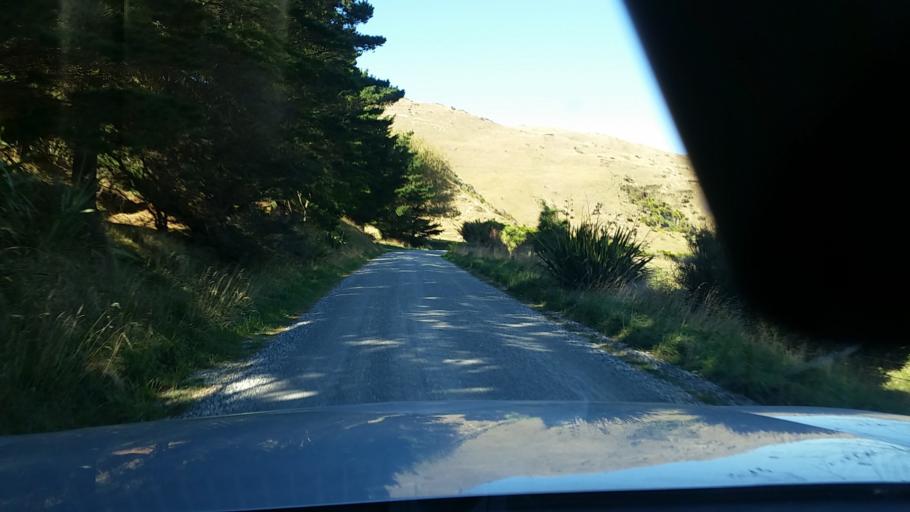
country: NZ
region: Marlborough
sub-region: Marlborough District
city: Blenheim
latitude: -41.8383
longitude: 174.1800
